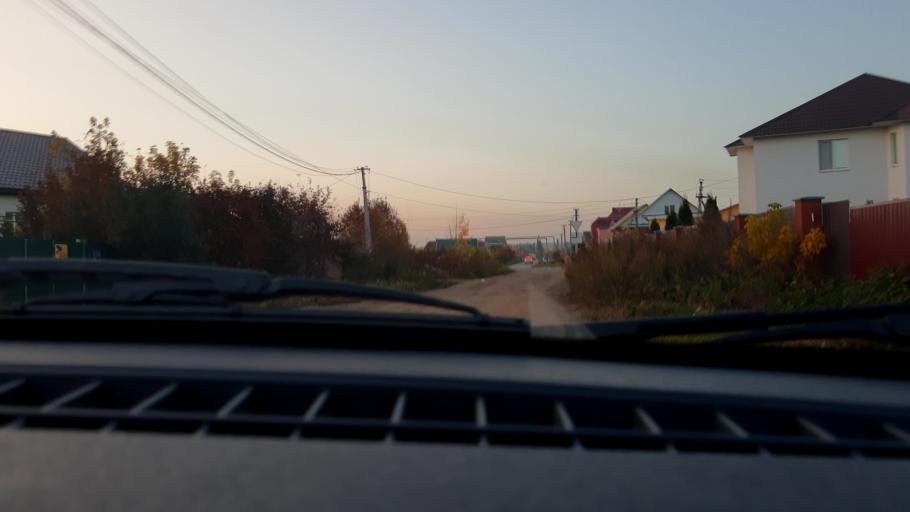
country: RU
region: Bashkortostan
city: Mikhaylovka
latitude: 54.7815
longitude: 55.9038
